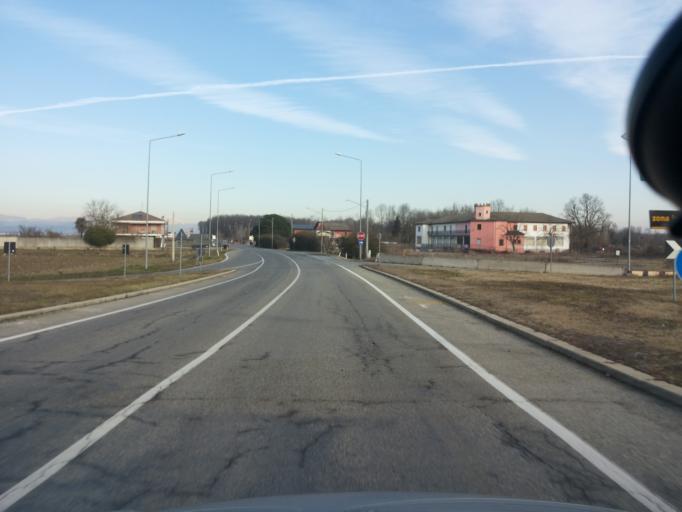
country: IT
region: Piedmont
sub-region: Provincia di Vercelli
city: Greggio
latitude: 45.4642
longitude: 8.3860
